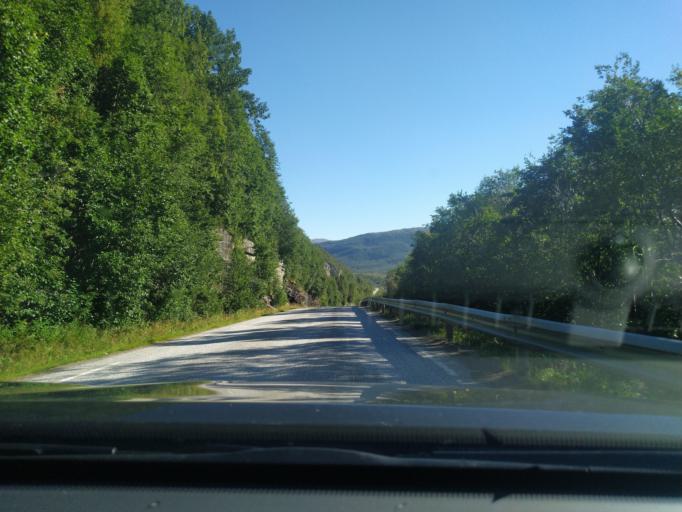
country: NO
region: Troms
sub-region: Dyroy
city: Brostadbotn
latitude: 68.9296
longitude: 17.6548
